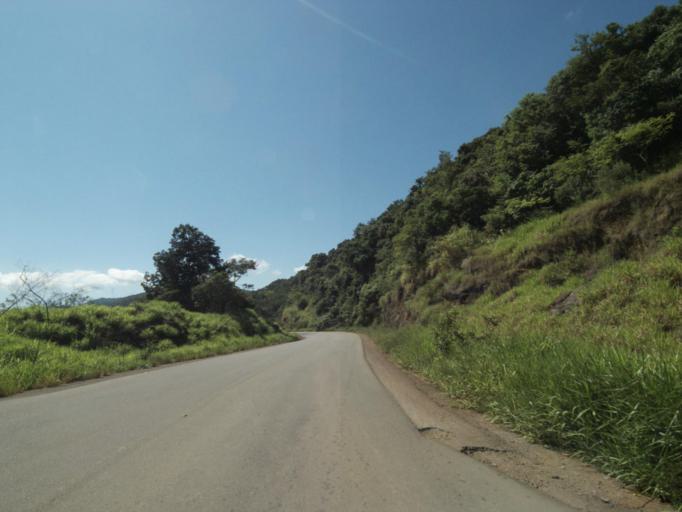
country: BR
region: Rio Grande do Sul
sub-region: Bento Goncalves
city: Bento Goncalves
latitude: -29.0906
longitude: -51.6375
